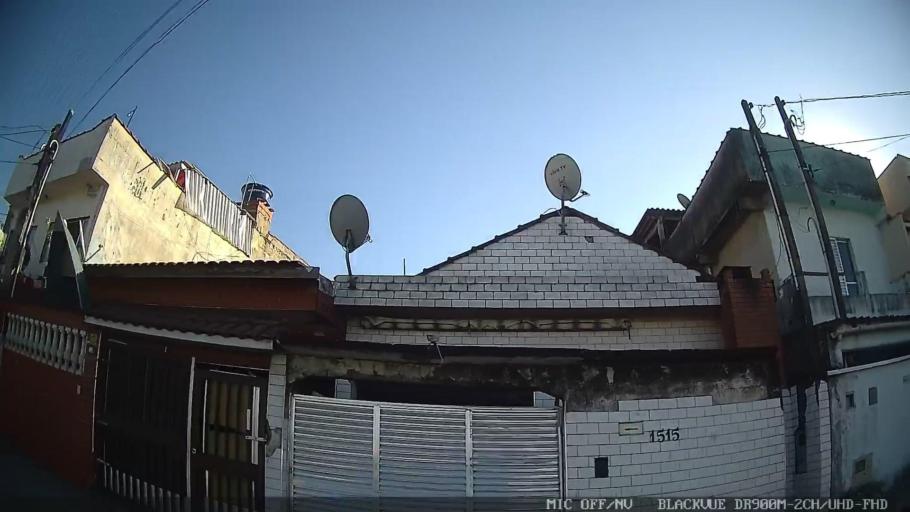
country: BR
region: Sao Paulo
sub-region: Guaruja
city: Guaruja
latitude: -23.9742
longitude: -46.2246
